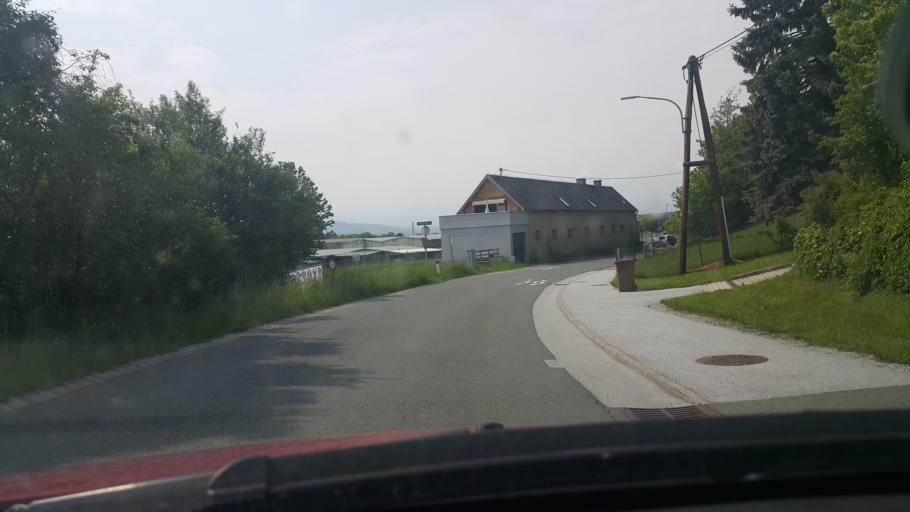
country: AT
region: Styria
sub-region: Politischer Bezirk Graz-Umgebung
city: Lieboch
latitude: 46.9666
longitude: 15.3479
